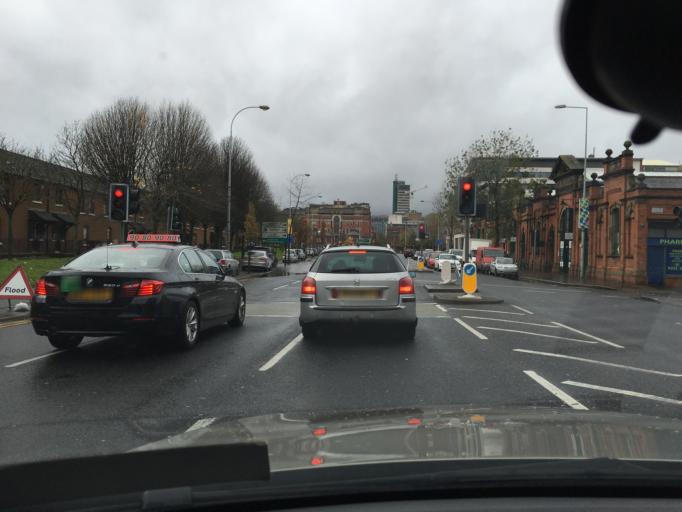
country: GB
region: Northern Ireland
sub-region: City of Belfast
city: Belfast
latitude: 54.5955
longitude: -5.9209
